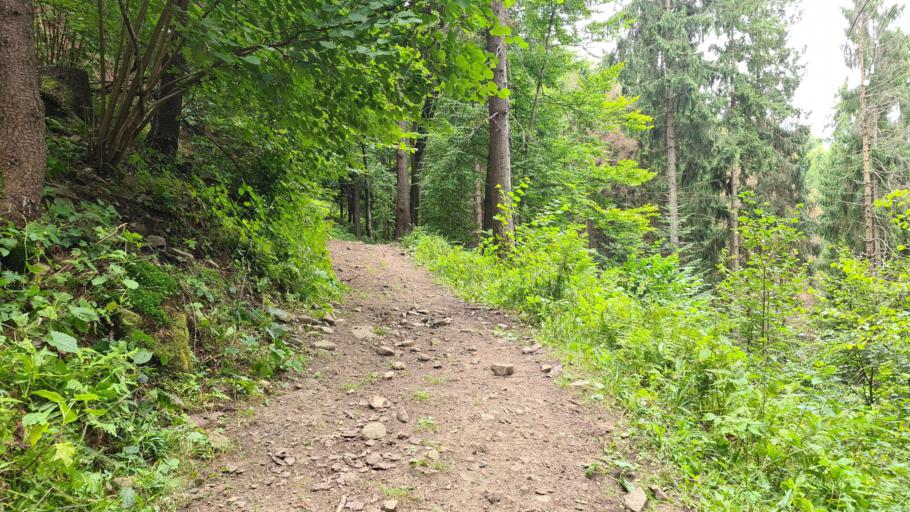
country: PL
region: Lesser Poland Voivodeship
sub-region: Powiat nowosadecki
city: Piwniczna-Zdroj
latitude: 49.4362
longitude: 20.7239
